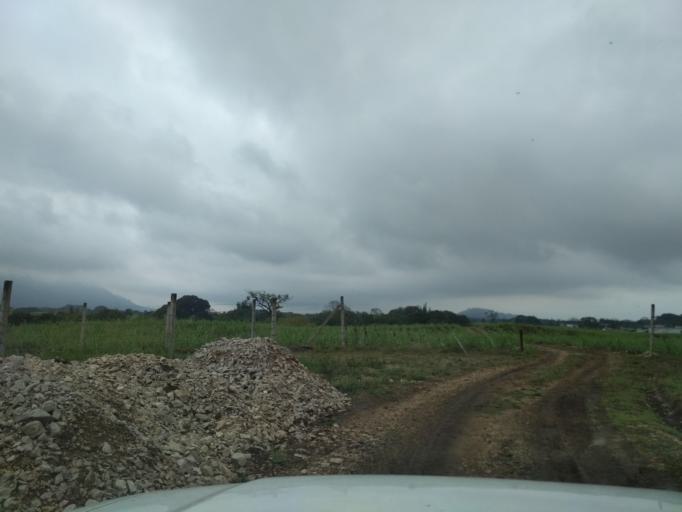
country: MX
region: Veracruz
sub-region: Cordoba
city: San Jose de Tapia
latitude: 18.8445
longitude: -96.9686
